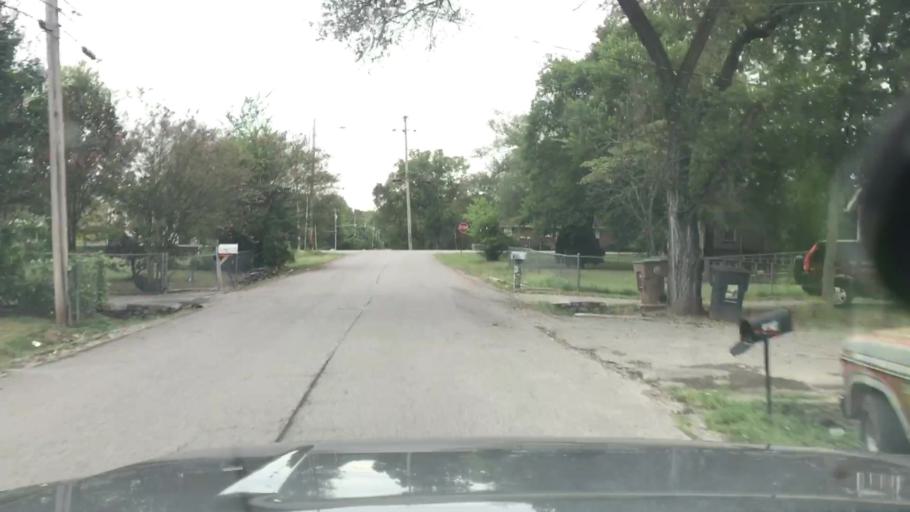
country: US
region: Tennessee
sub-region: Davidson County
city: Nashville
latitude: 36.2105
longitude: -86.8406
